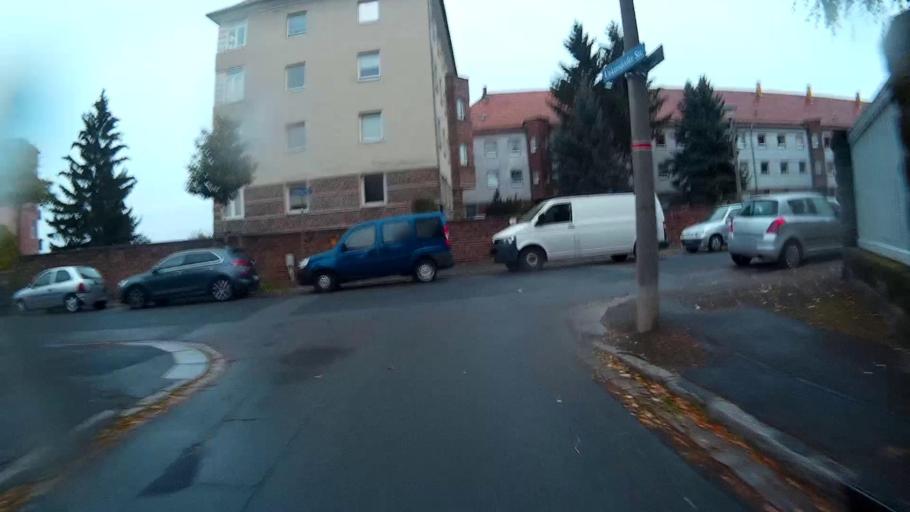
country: DE
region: Saxony
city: Dresden
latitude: 51.0500
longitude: 13.6941
